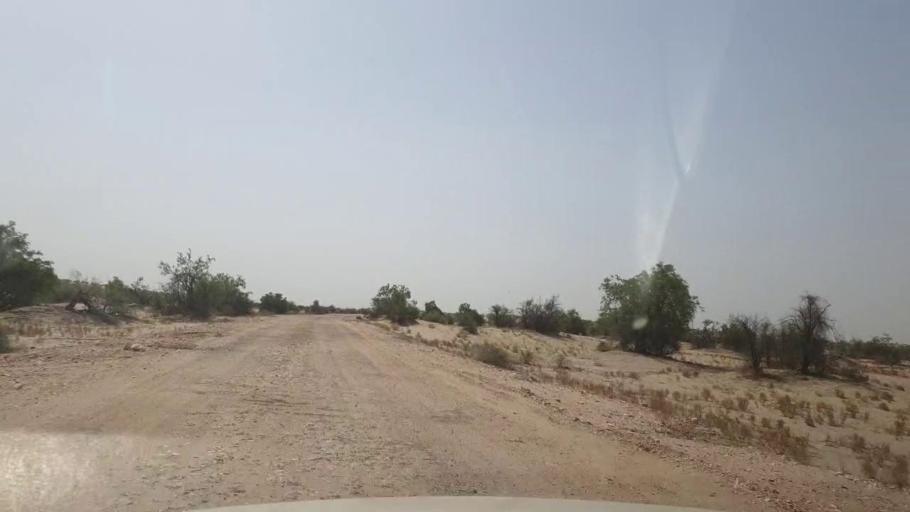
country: PK
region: Sindh
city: Rohri
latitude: 27.4414
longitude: 69.2411
